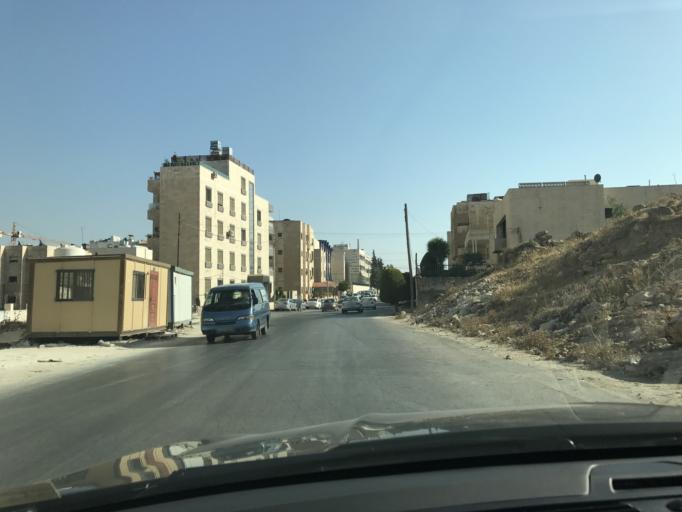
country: JO
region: Amman
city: Wadi as Sir
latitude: 31.9504
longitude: 35.8524
